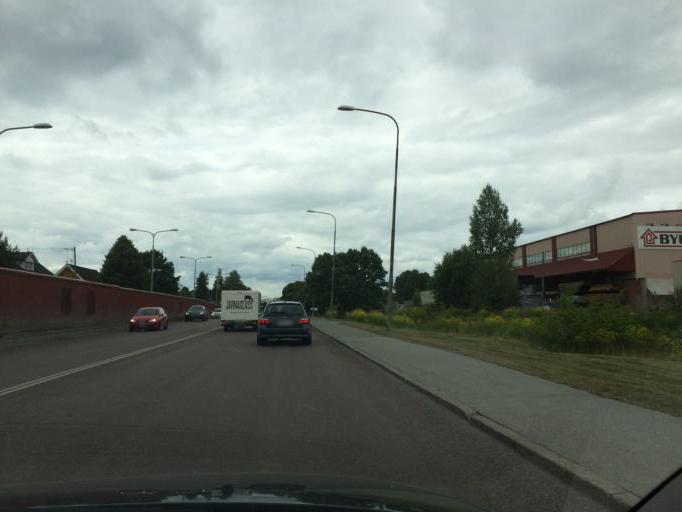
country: SE
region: Stockholm
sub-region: Stockholms Kommun
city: Kista
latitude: 59.3739
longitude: 17.9172
